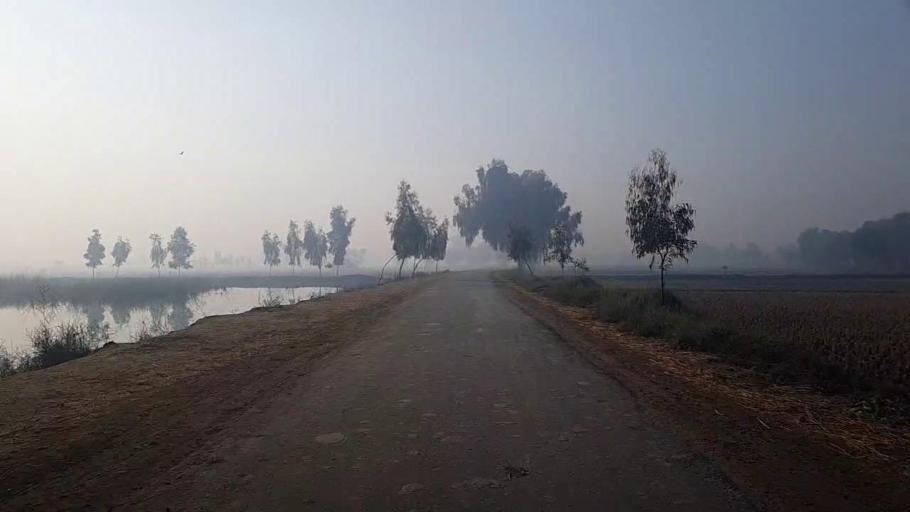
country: PK
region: Sindh
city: Mehar
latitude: 27.1460
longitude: 67.8229
